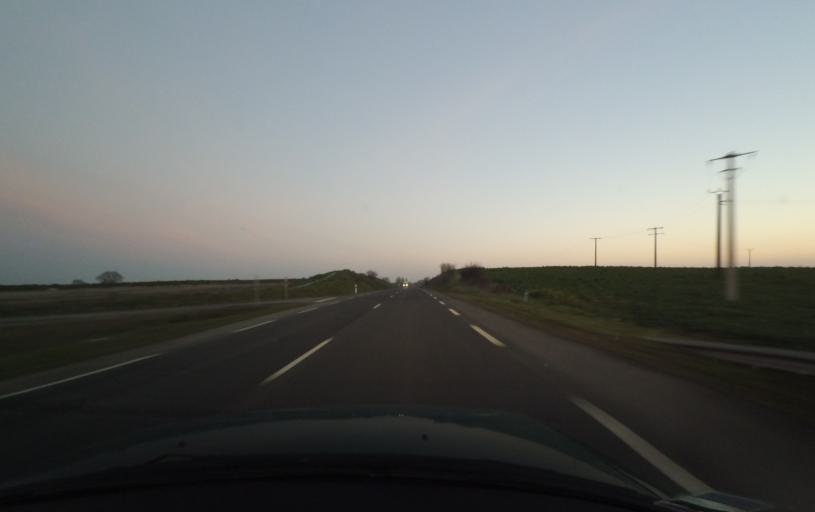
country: FR
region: Pays de la Loire
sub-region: Departement de la Mayenne
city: Soulge-sur-Ouette
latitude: 48.0438
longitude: -0.5739
